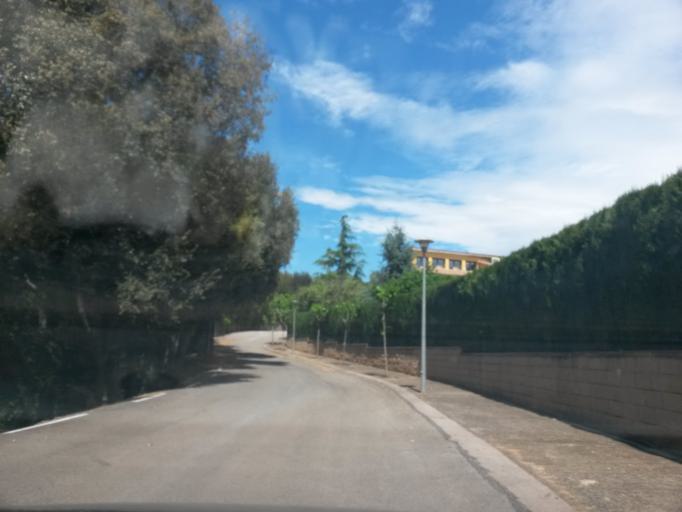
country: ES
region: Catalonia
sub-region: Provincia de Girona
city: Vilablareix
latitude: 41.9600
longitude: 2.7602
